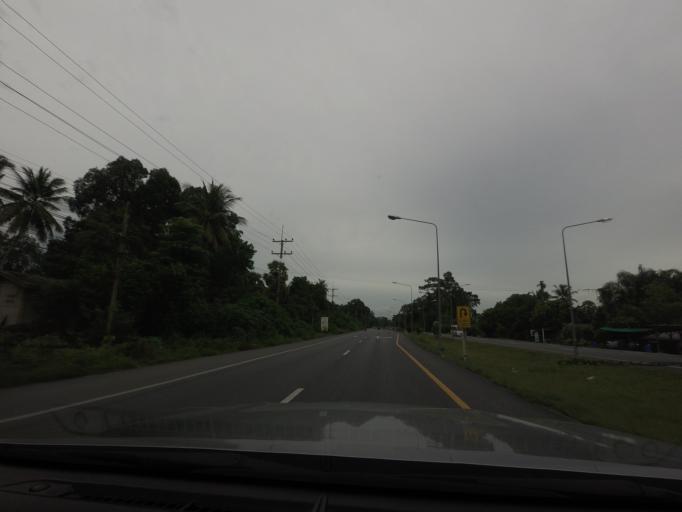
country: TH
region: Nakhon Si Thammarat
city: Chaloem Phra Kiat
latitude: 8.2317
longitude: 100.0194
